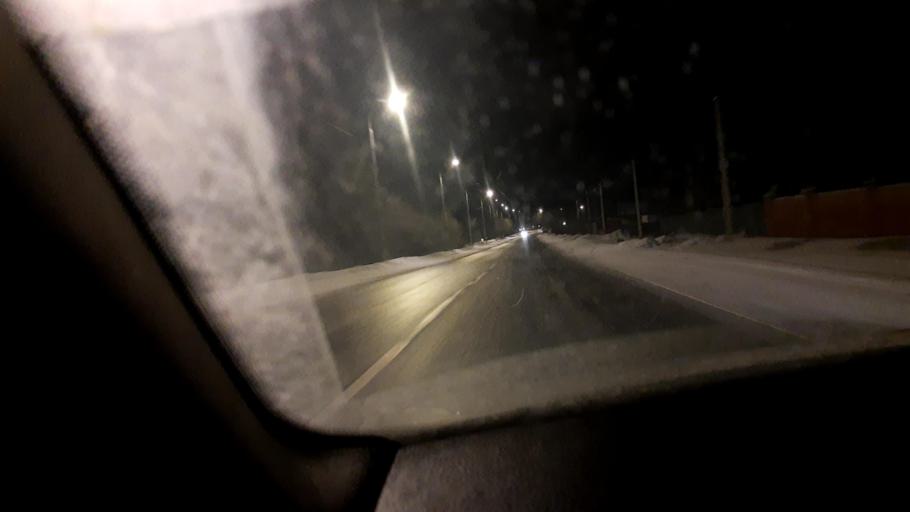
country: RU
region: Moskovskaya
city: Shemetovo
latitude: 56.5172
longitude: 38.1166
